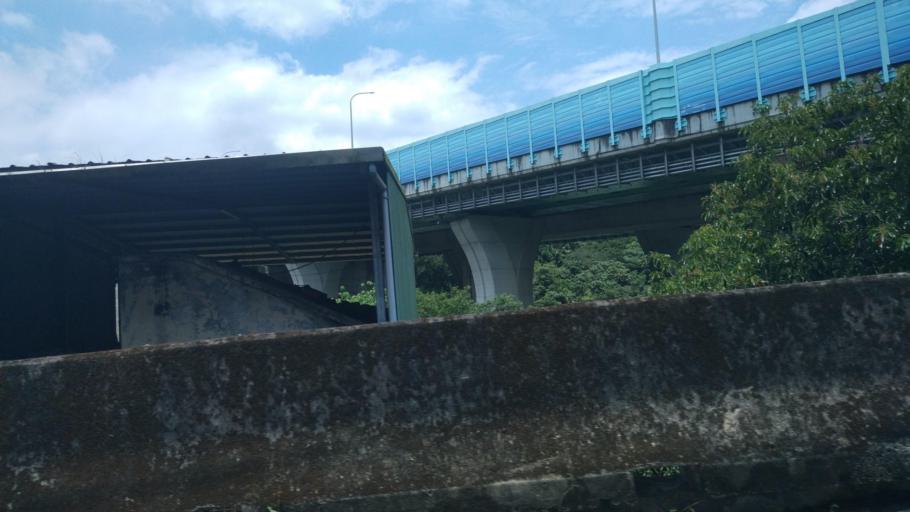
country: TW
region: Taipei
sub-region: Taipei
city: Banqiao
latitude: 24.9486
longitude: 121.4922
